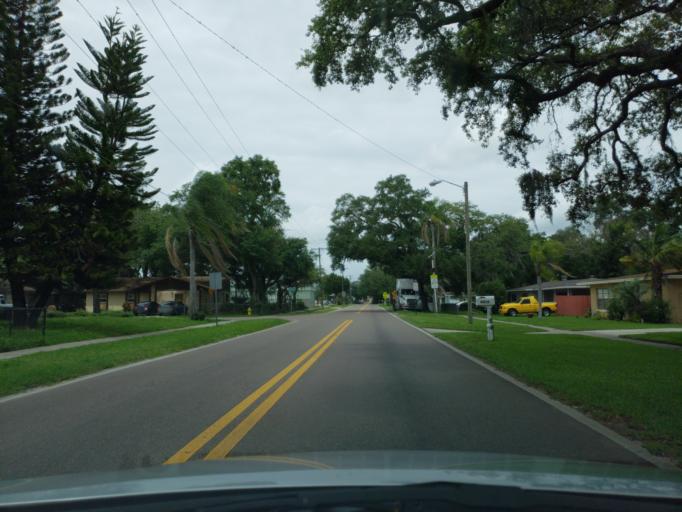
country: US
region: Florida
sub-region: Hillsborough County
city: Temple Terrace
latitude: 28.0107
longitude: -82.4072
